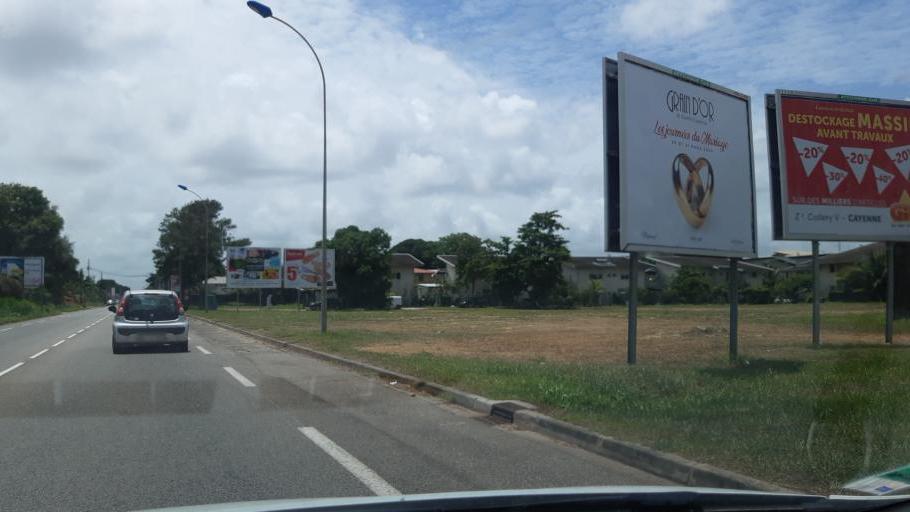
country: GF
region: Guyane
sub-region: Guyane
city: Remire-Montjoly
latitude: 4.9167
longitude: -52.2763
